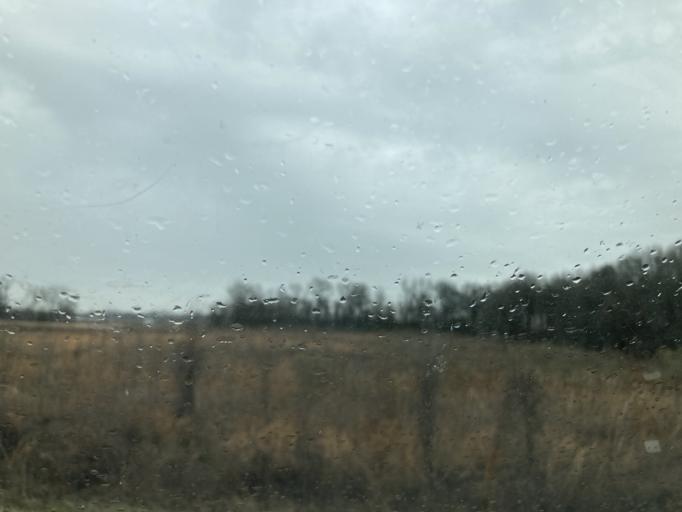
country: US
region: Mississippi
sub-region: Humphreys County
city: Belzoni
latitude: 33.0522
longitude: -90.4699
